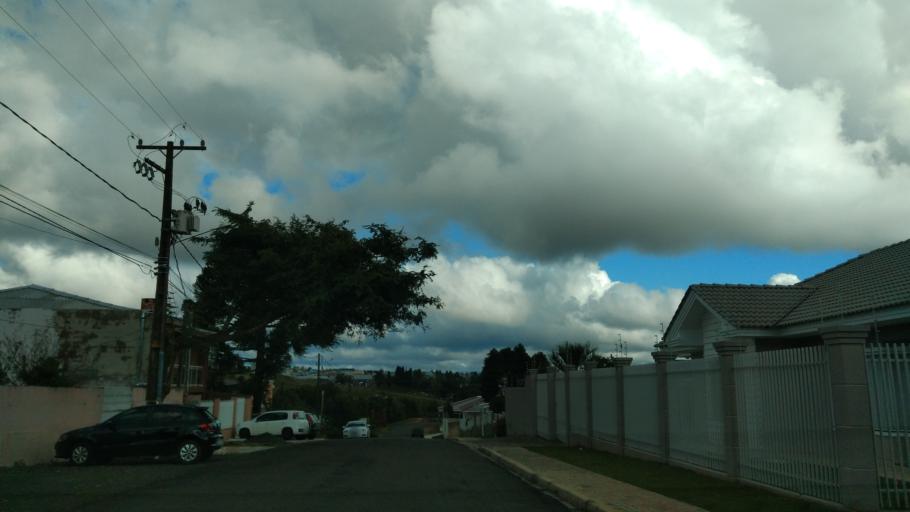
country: BR
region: Parana
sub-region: Guarapuava
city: Guarapuava
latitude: -25.3961
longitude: -51.4885
